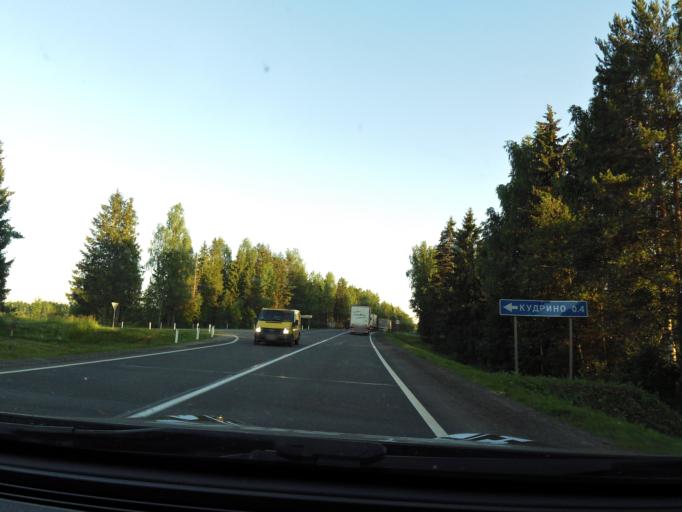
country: RU
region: Jaroslavl
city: Prechistoye
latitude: 58.4533
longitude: 40.3218
